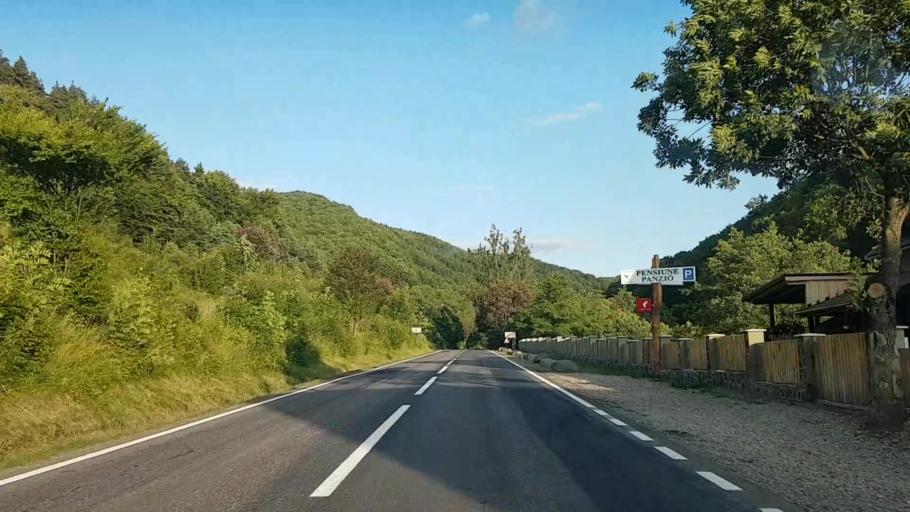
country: RO
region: Harghita
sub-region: Comuna Corund
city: Corund
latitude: 46.4656
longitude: 25.2049
